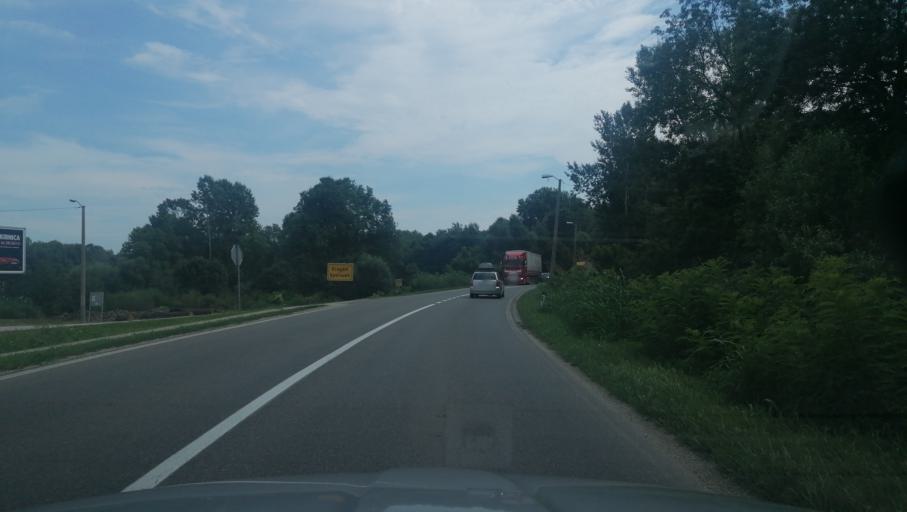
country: BA
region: Brcko
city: Brcko
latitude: 44.9261
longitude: 18.7323
